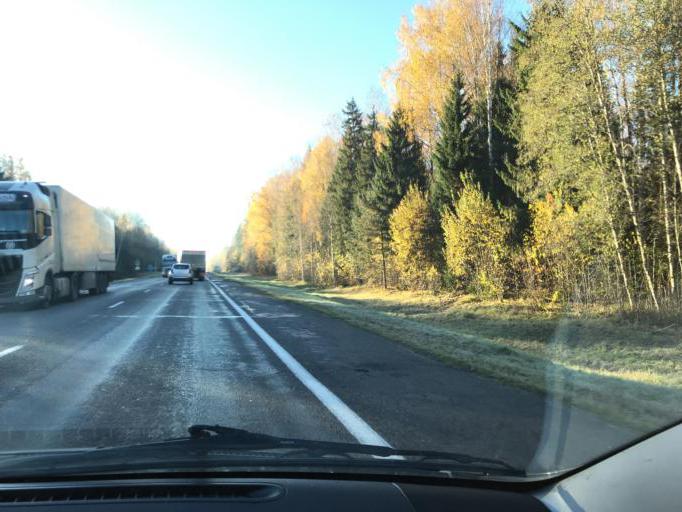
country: BY
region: Vitebsk
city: Vitebsk
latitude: 54.9515
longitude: 30.3600
